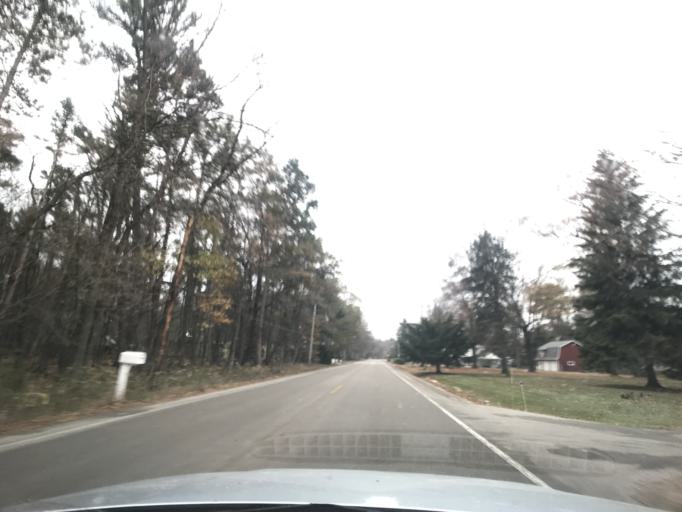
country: US
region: Wisconsin
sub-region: Marinette County
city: Marinette
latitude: 45.0660
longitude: -87.6193
